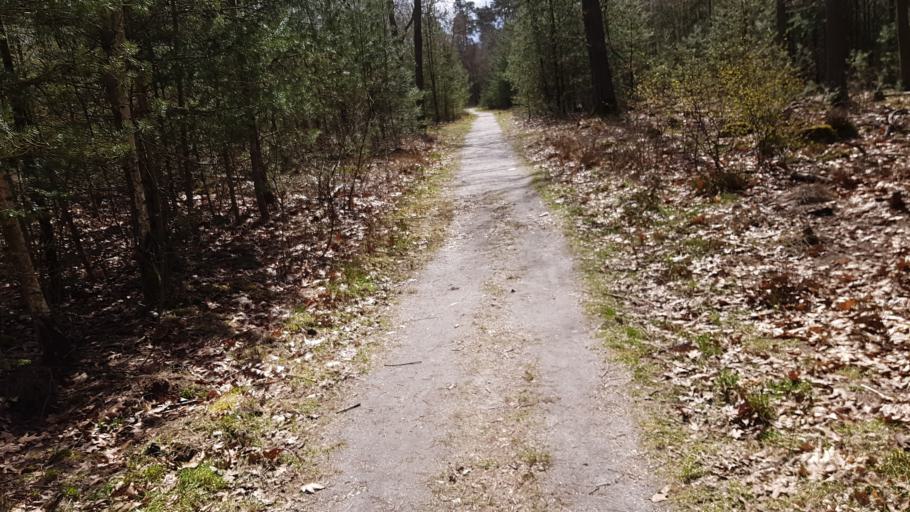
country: NL
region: Gelderland
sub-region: Gemeente Epe
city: Vaassen
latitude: 52.3110
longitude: 5.9221
